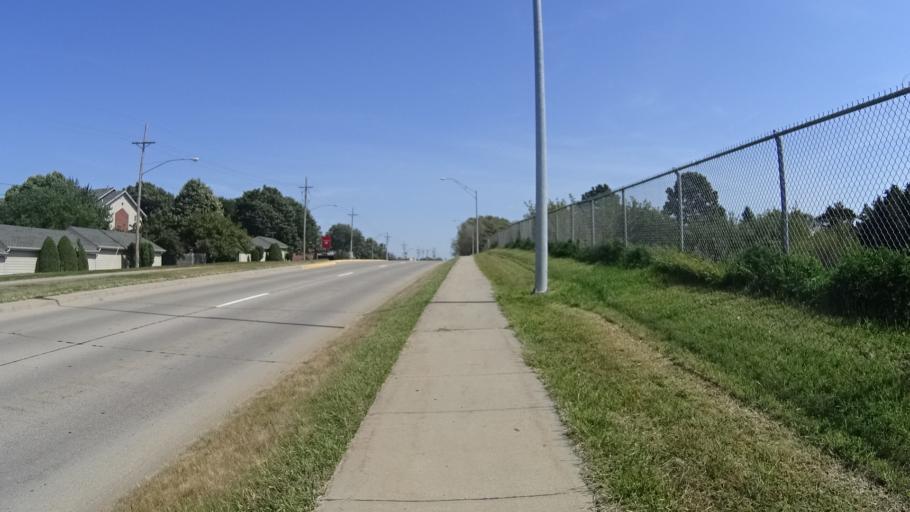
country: US
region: Nebraska
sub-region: Sarpy County
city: La Vista
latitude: 41.1761
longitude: -96.0502
